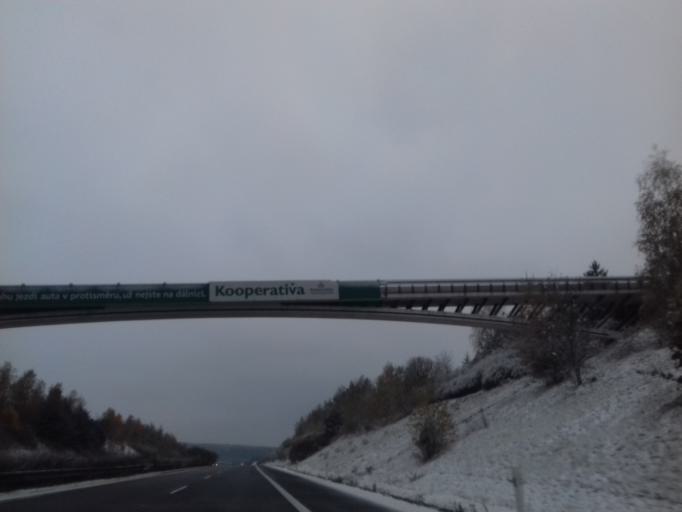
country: CZ
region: Plzensky
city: Zbiroh
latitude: 49.8212
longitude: 13.7694
